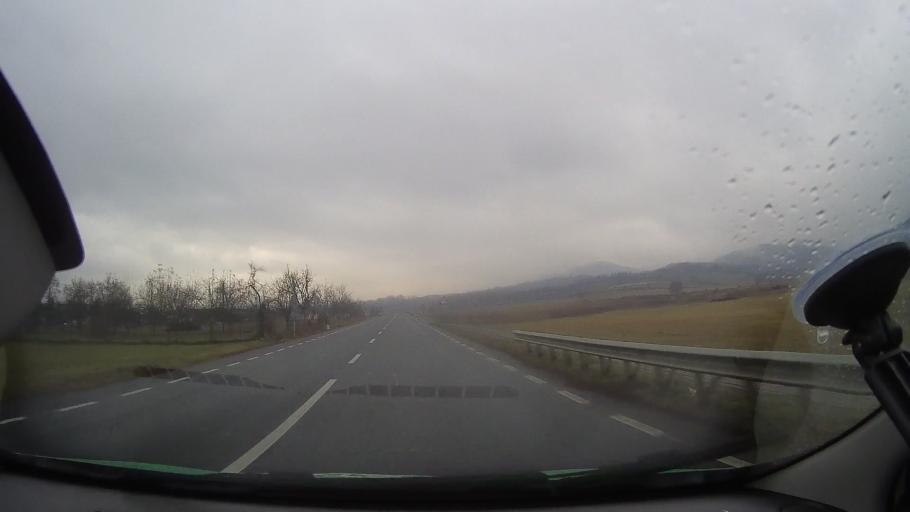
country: RO
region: Hunedoara
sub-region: Comuna Baia de Cris
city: Baia de Cris
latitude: 46.1766
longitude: 22.7075
